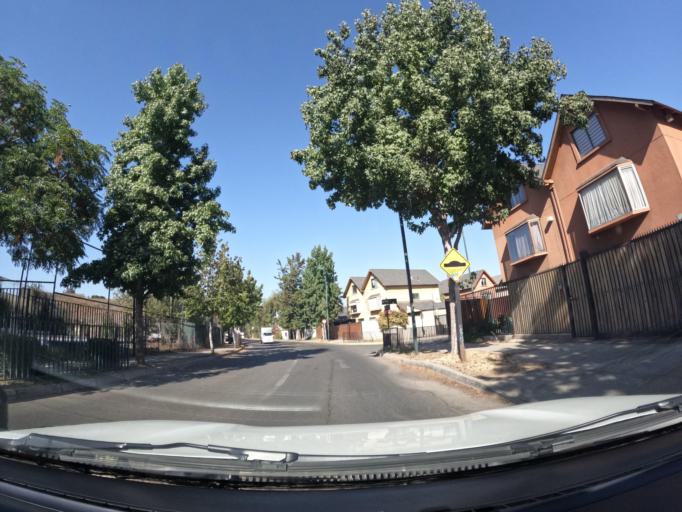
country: CL
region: Santiago Metropolitan
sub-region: Provincia de Santiago
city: Villa Presidente Frei, Nunoa, Santiago, Chile
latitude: -33.4929
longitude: -70.5781
